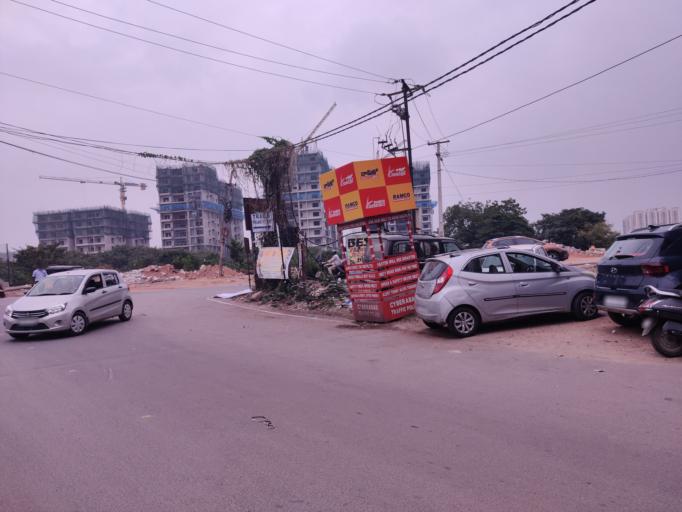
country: IN
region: Telangana
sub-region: Hyderabad
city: Hyderabad
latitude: 17.4088
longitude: 78.3945
